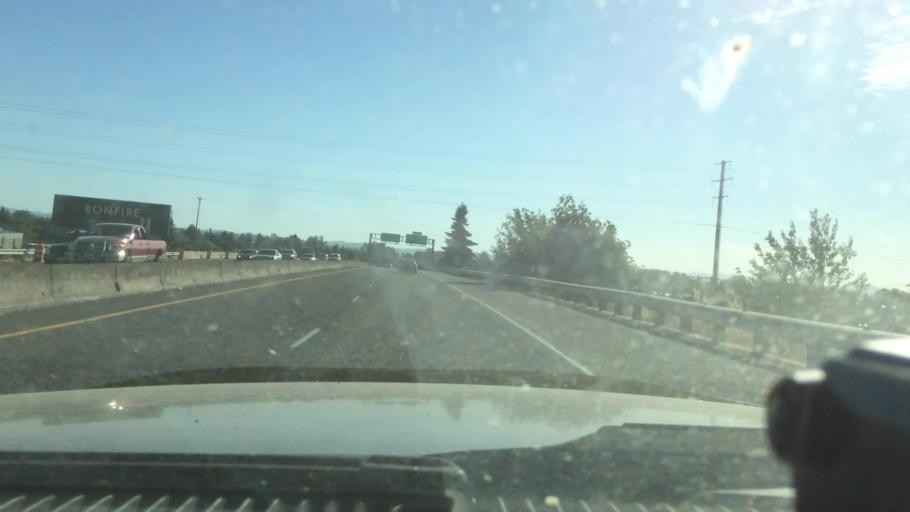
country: US
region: Oregon
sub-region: Lane County
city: Eugene
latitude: 44.0973
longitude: -123.1643
